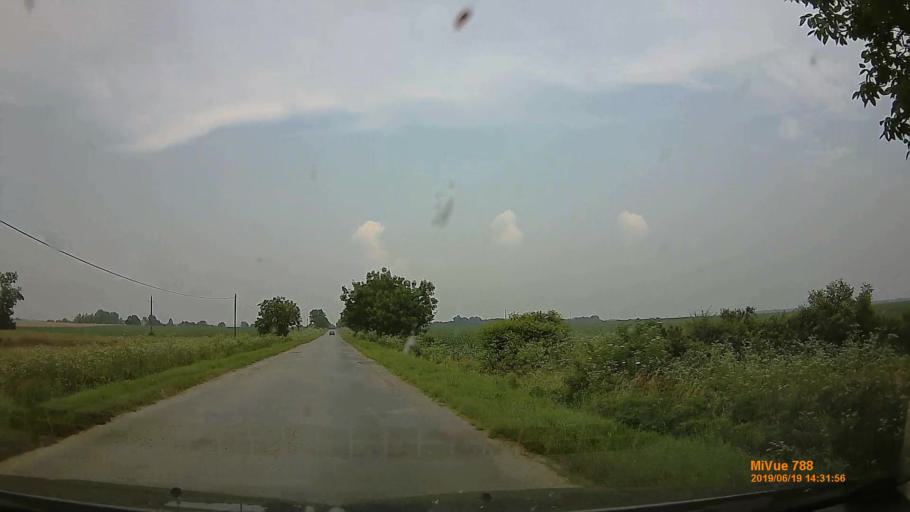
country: HU
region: Baranya
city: Szigetvar
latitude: 46.0726
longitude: 17.7693
